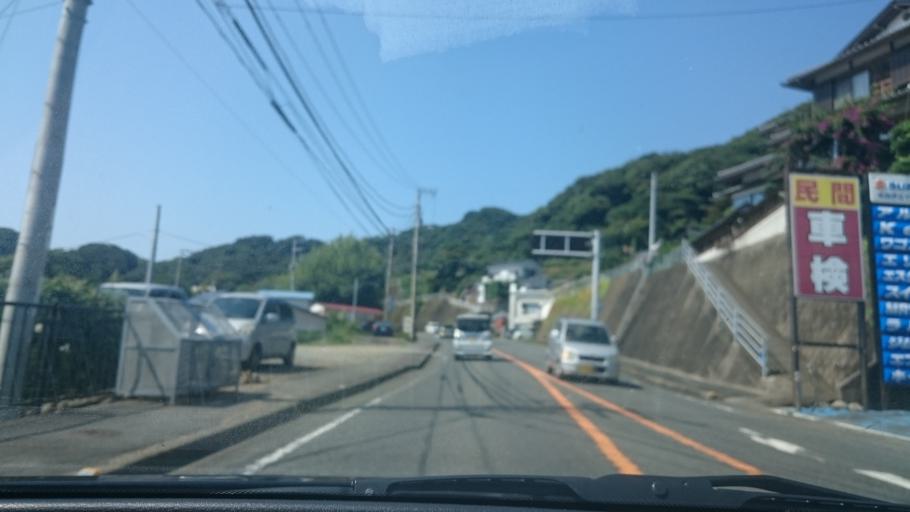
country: JP
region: Shizuoka
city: Heda
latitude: 34.8113
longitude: 138.7728
